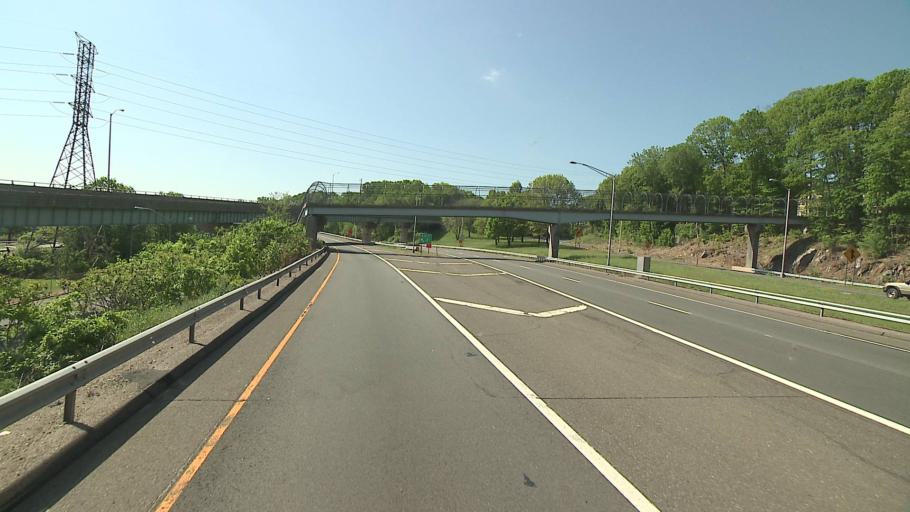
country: US
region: Connecticut
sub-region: New Haven County
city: Waterbury
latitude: 41.5542
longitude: -73.0551
